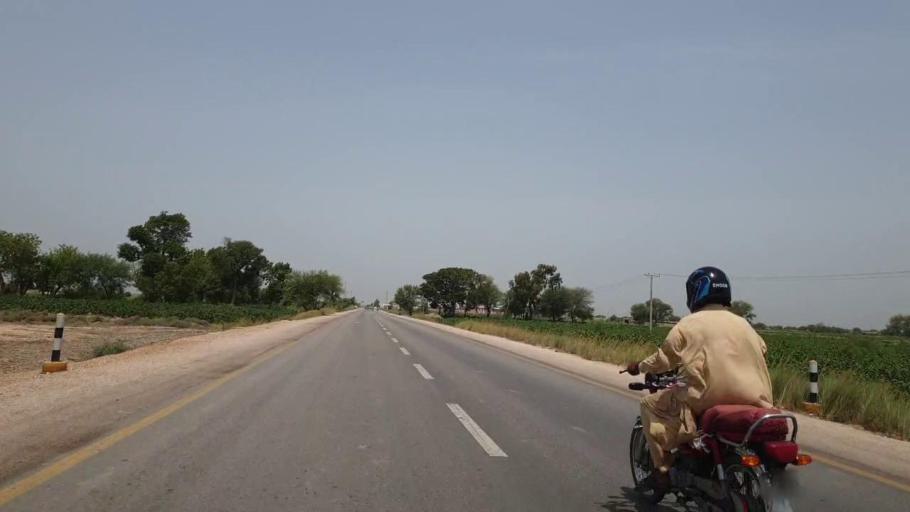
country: PK
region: Sindh
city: Shahpur Chakar
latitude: 26.1935
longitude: 68.5725
